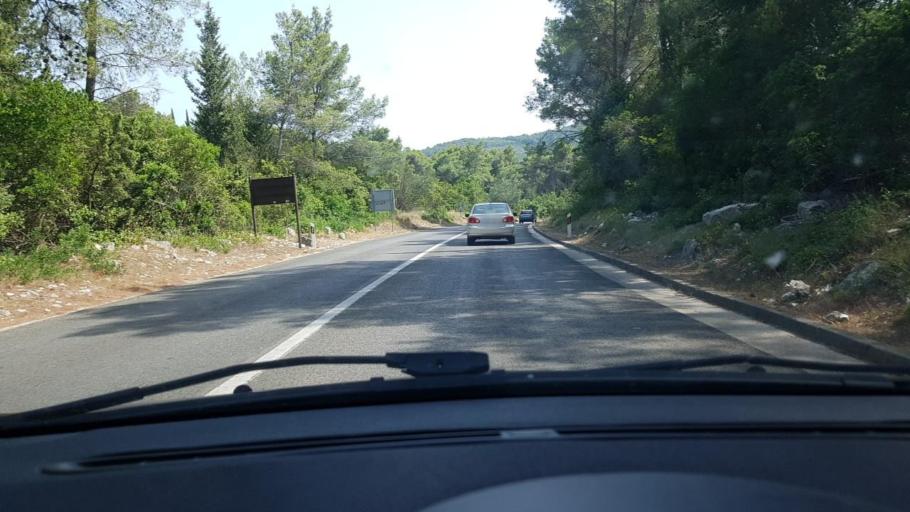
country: HR
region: Dubrovacko-Neretvanska
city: Korcula
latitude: 42.9532
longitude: 17.1314
